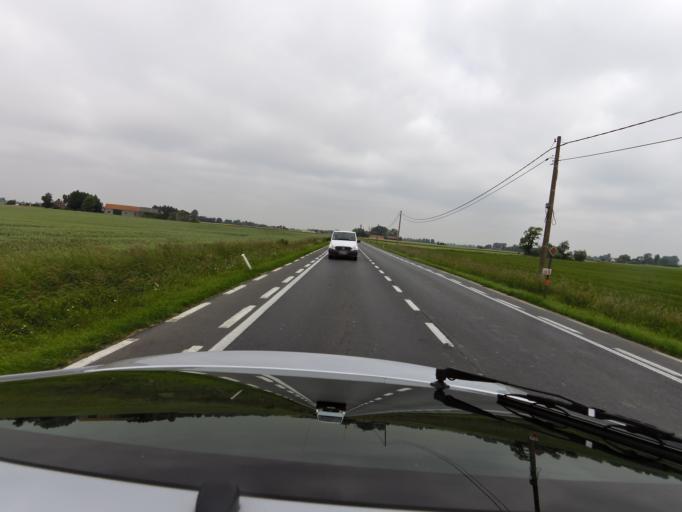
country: BE
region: Flanders
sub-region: Provincie West-Vlaanderen
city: Alveringem
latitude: 51.0089
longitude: 2.6831
